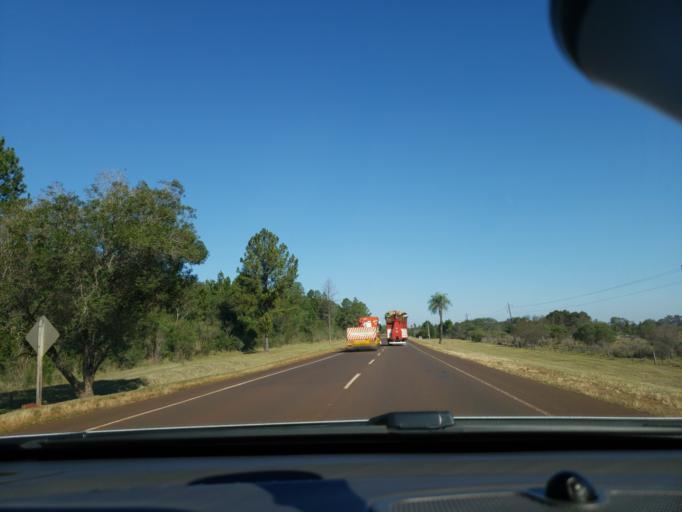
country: AR
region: Misiones
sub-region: Departamento de Apostoles
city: San Jose
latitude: -27.8205
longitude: -55.7699
